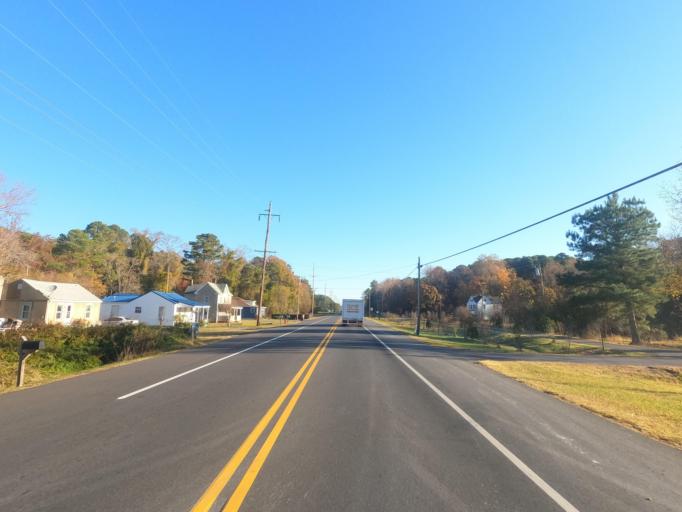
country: US
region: Maryland
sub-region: Somerset County
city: Crisfield
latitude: 37.9963
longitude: -75.8363
